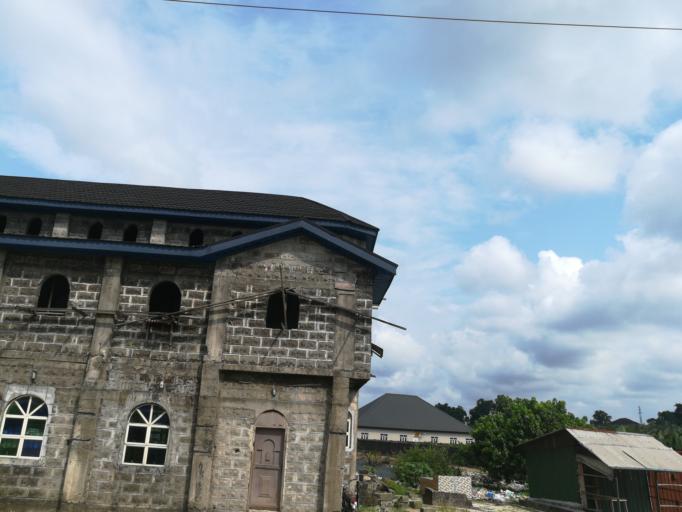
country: NG
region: Rivers
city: Okrika
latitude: 4.7455
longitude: 7.0976
